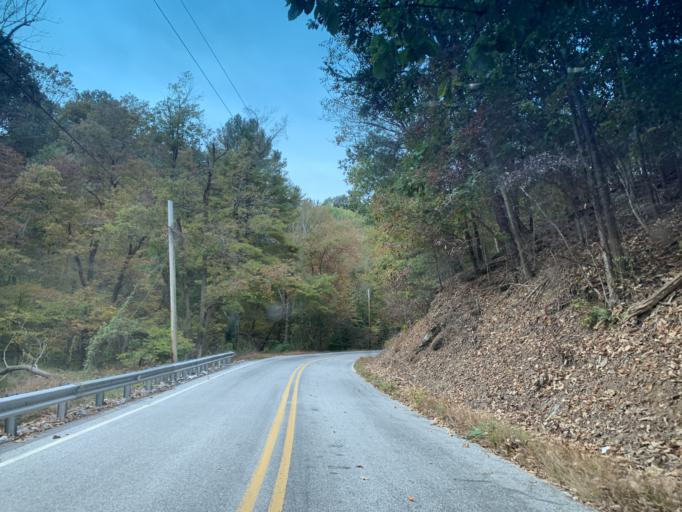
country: US
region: Pennsylvania
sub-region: York County
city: Windsor
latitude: 39.8330
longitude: -76.5157
